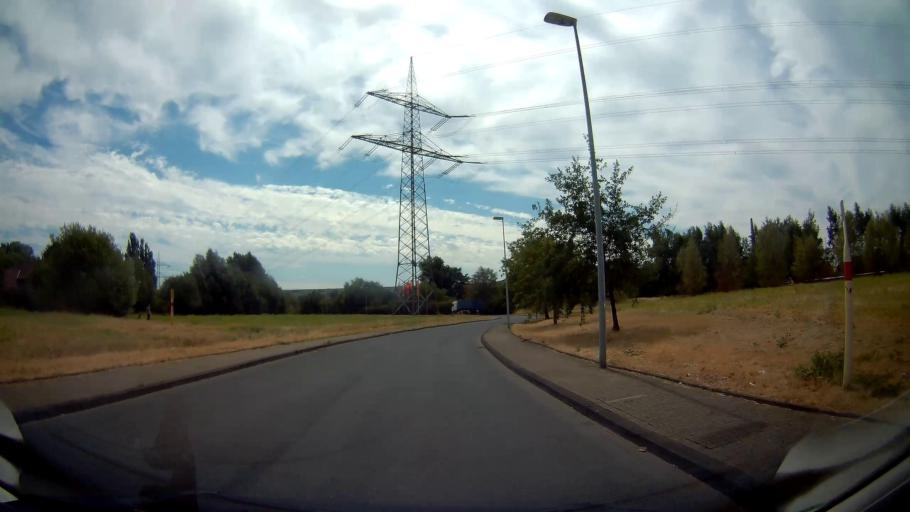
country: DE
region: North Rhine-Westphalia
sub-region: Regierungsbezirk Munster
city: Gelsenkirchen
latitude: 51.5270
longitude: 7.0797
